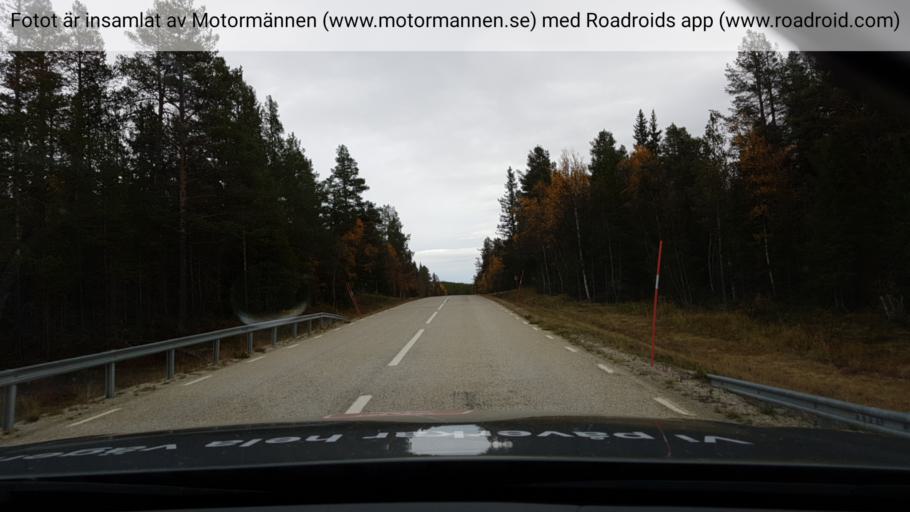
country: SE
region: Jaemtland
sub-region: Are Kommun
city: Are
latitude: 62.8260
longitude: 12.9138
